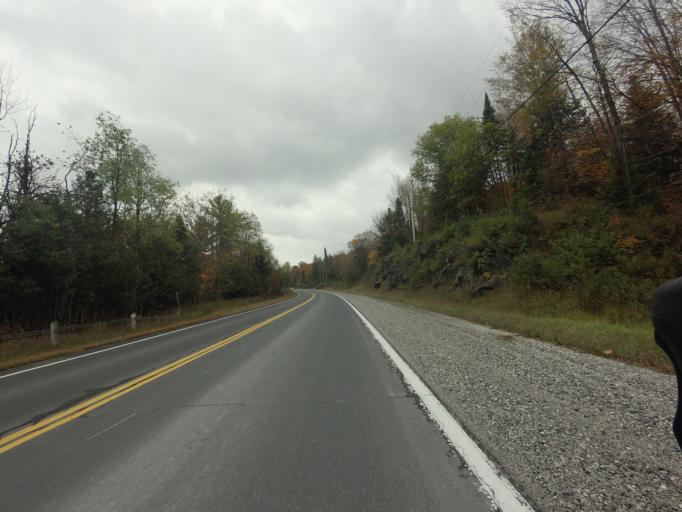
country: CA
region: Ontario
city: Perth
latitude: 45.1163
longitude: -76.4908
